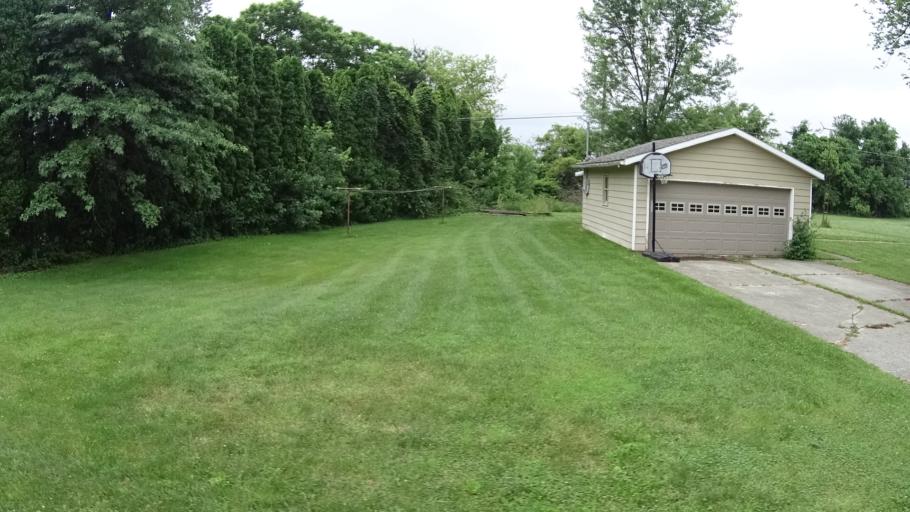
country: US
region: Ohio
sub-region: Erie County
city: Milan
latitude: 41.2962
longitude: -82.5552
